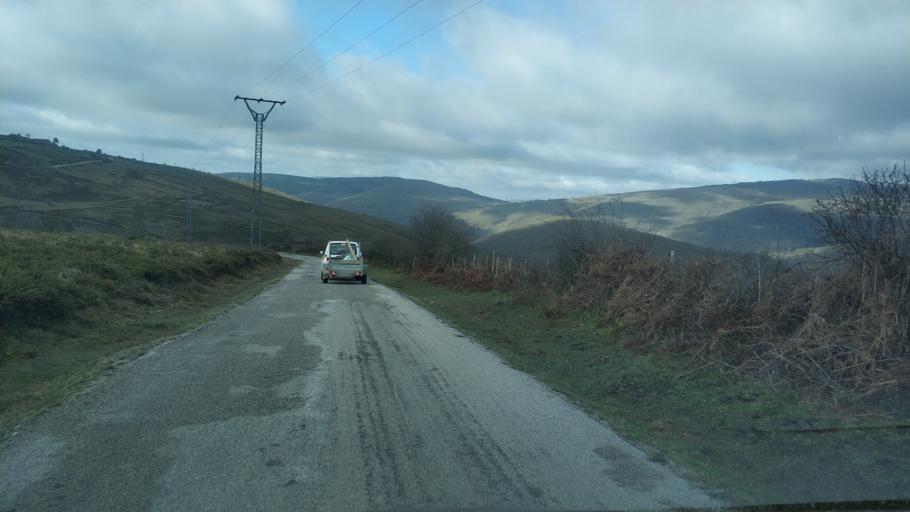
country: ES
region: Castille and Leon
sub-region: Provincia de Burgos
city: Arija
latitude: 42.9162
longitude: -3.9999
